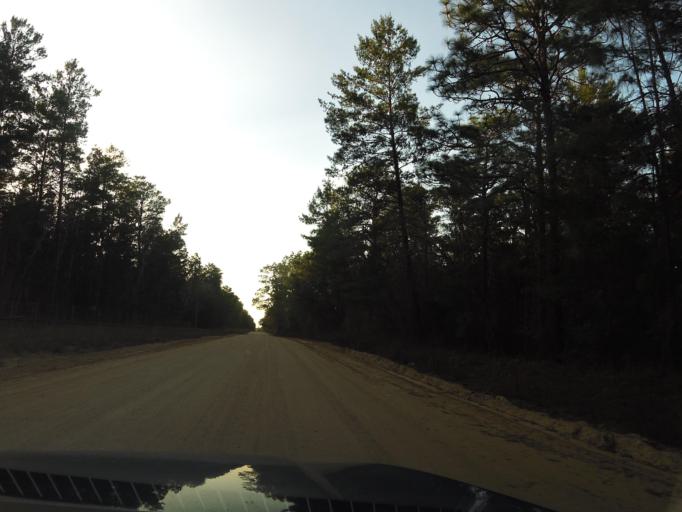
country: US
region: Florida
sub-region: Putnam County
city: Interlachen
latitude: 29.7845
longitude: -81.8658
